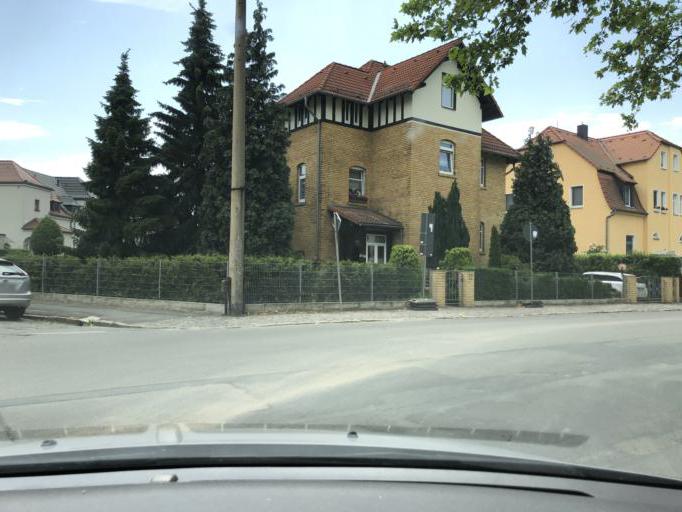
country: DE
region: Saxony
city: Taucha
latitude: 51.3810
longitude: 12.4865
